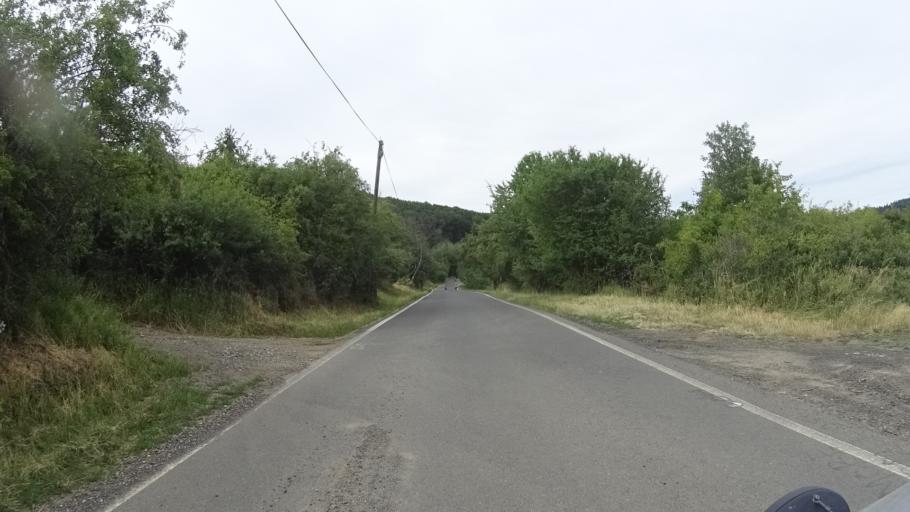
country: CZ
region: Ustecky
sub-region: Okres Litomerice
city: Litomerice
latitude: 50.5659
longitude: 14.1206
